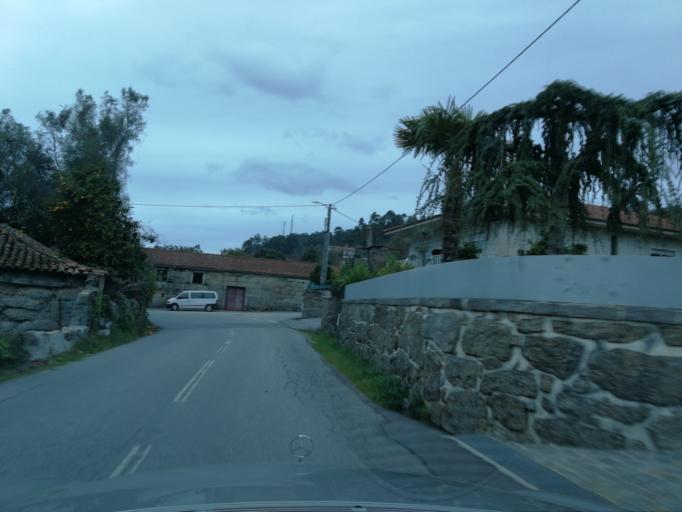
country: PT
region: Braga
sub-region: Braga
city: Oliveira
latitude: 41.4823
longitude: -8.4708
